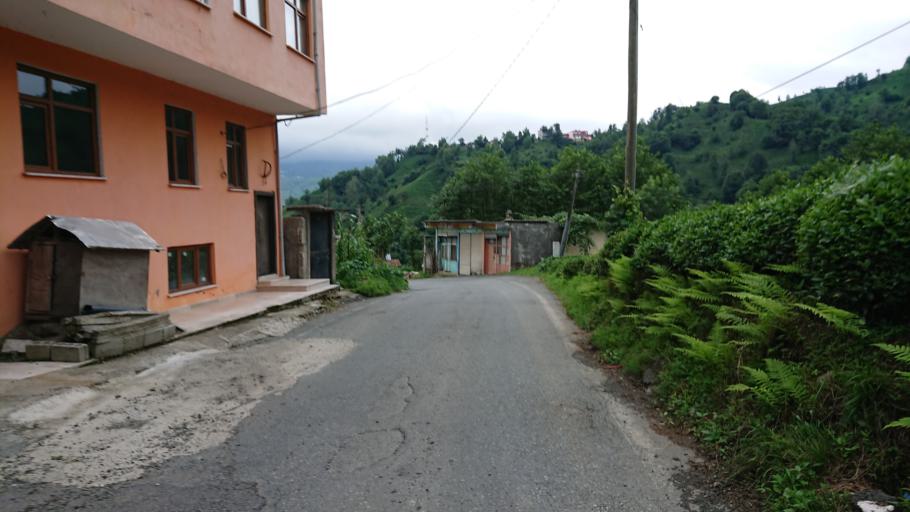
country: TR
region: Rize
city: Rize
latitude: 40.9655
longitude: 40.5150
